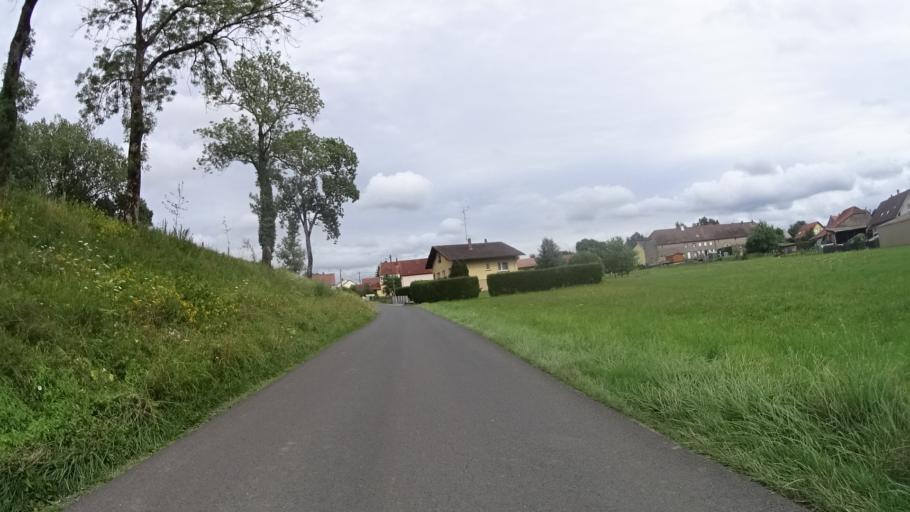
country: FR
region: Lorraine
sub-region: Departement de la Moselle
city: Niderviller
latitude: 48.7070
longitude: 7.0757
